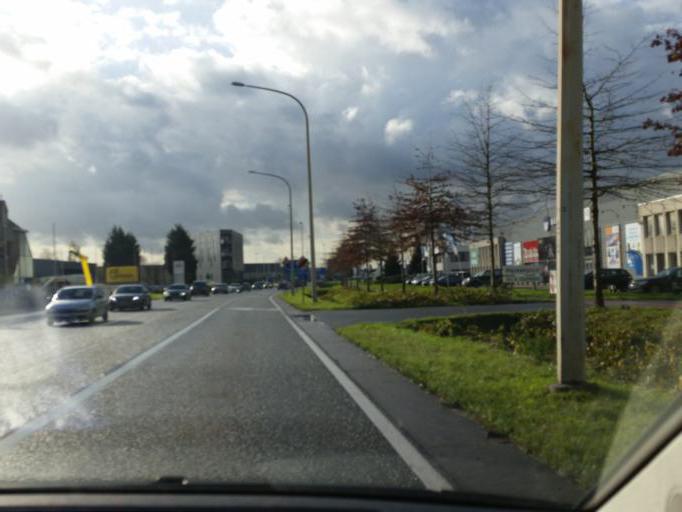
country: BE
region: Flanders
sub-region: Provincie Vlaams-Brabant
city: Vilvoorde
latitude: 50.9480
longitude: 4.4467
